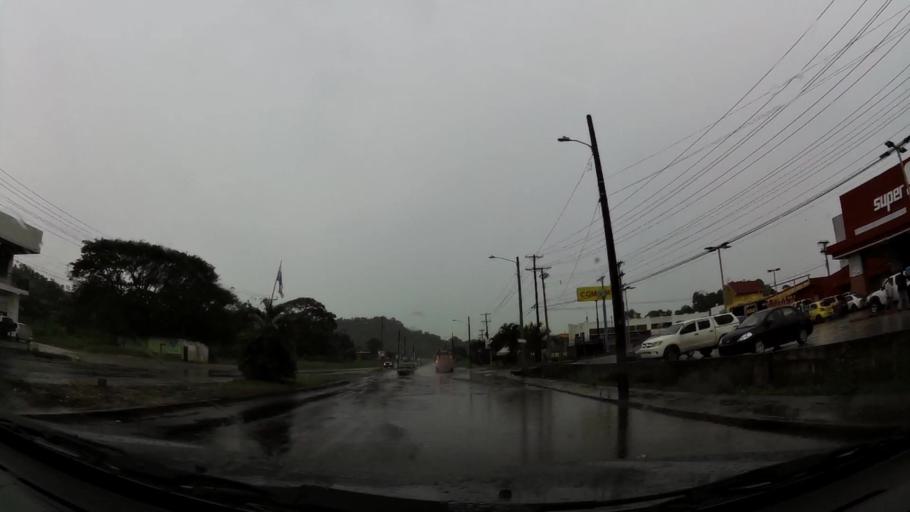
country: PA
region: Colon
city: Sabanitas
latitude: 9.3486
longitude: -79.8098
